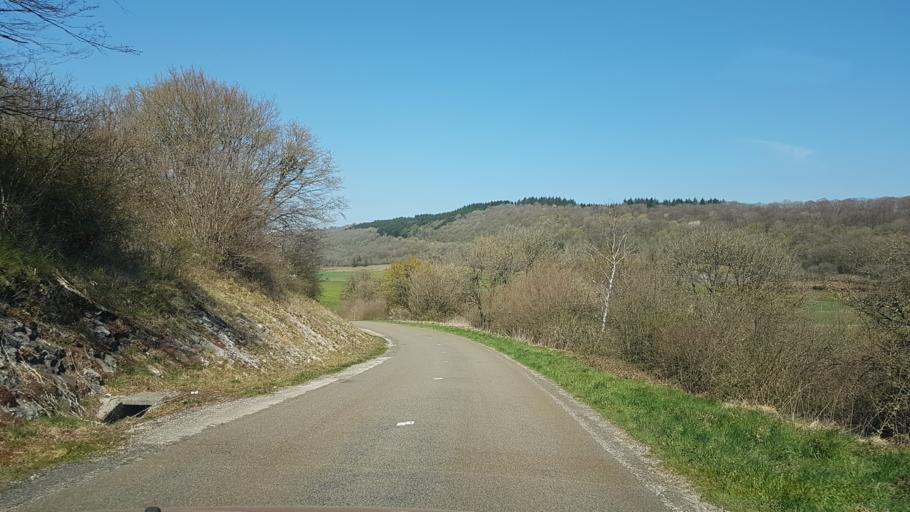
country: FR
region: Franche-Comte
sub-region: Departement du Jura
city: Orgelet
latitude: 46.5078
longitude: 5.5295
